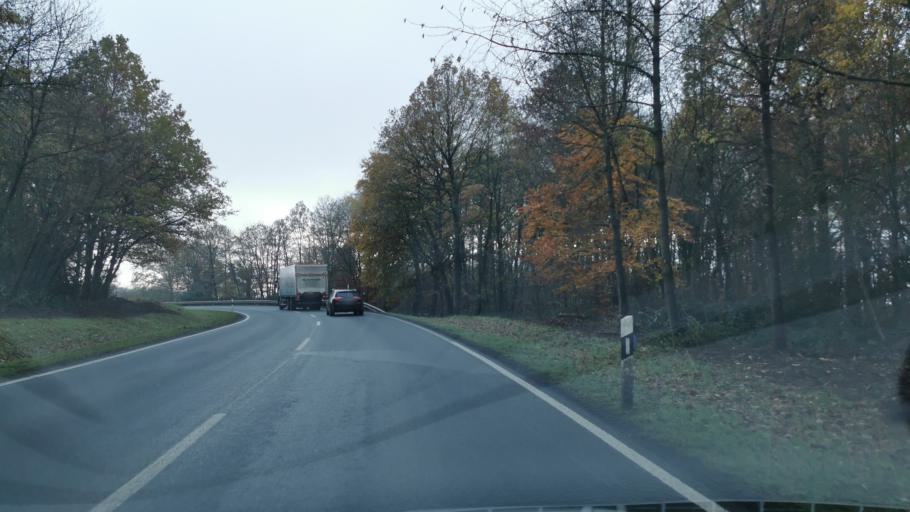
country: DE
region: Rheinland-Pfalz
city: Faid
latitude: 50.1579
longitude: 7.1101
